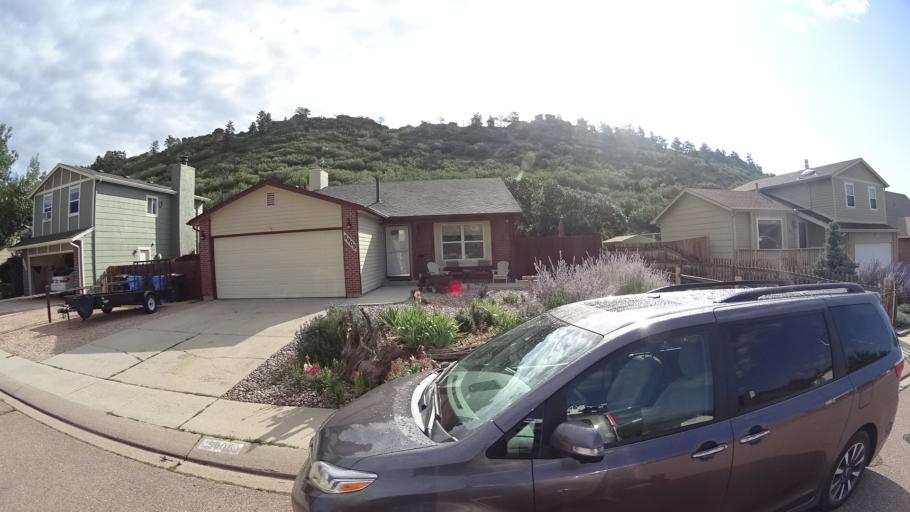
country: US
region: Colorado
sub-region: El Paso County
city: Air Force Academy
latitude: 38.9161
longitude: -104.8599
